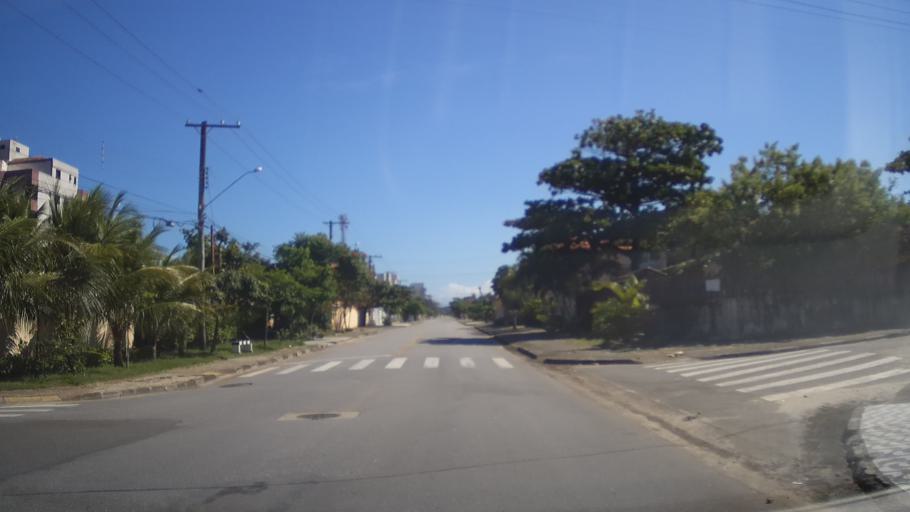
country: BR
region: Sao Paulo
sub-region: Mongagua
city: Mongagua
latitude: -24.1281
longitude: -46.6850
